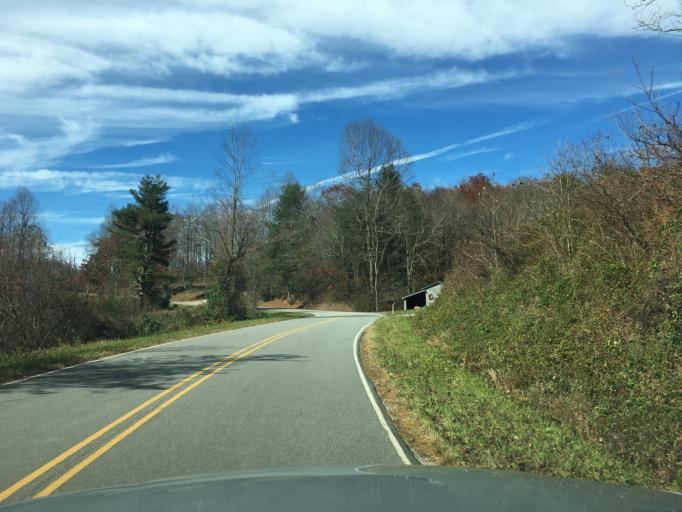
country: US
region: North Carolina
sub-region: Henderson County
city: Valley Hill
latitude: 35.2278
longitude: -82.5012
